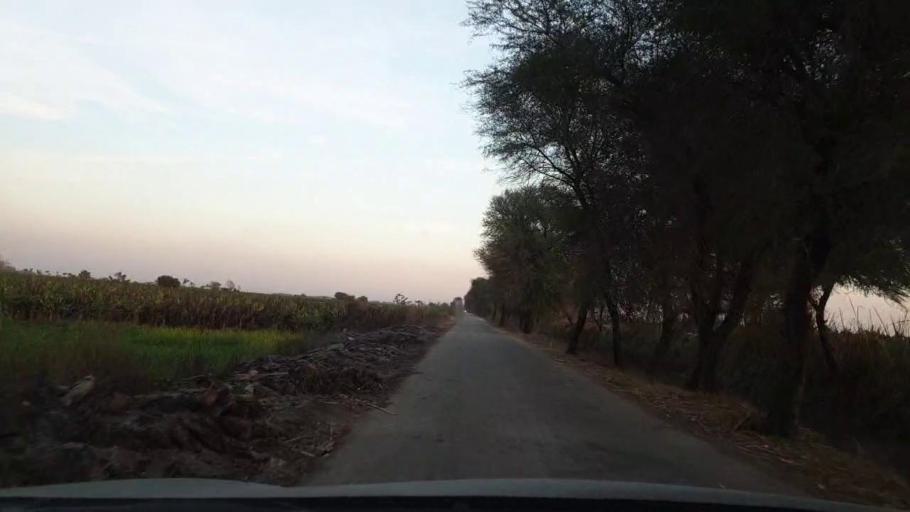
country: PK
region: Sindh
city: Tando Allahyar
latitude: 25.5951
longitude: 68.7046
